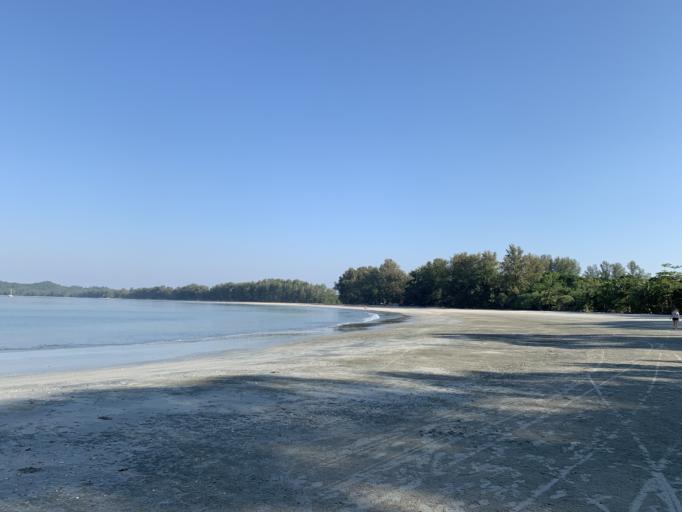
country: TH
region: Ranong
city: Kapoe
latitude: 9.7110
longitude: 98.3966
